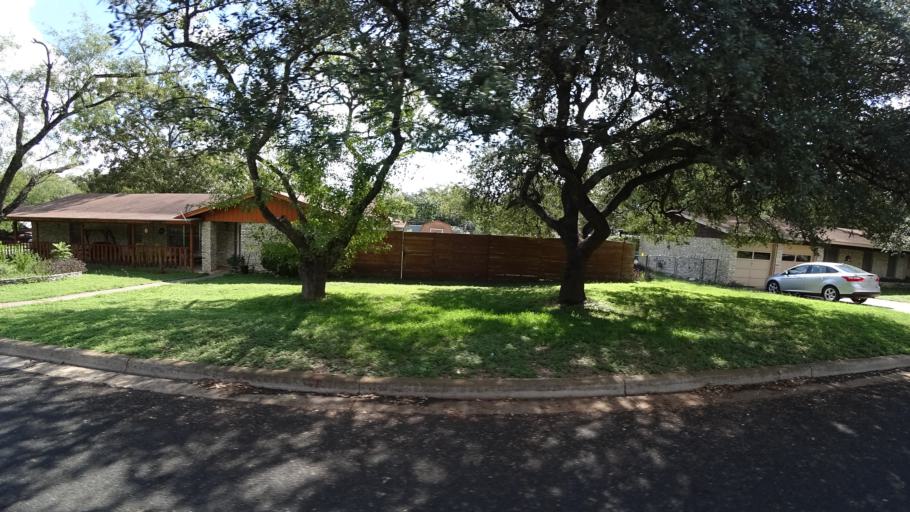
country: US
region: Texas
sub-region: Travis County
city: Shady Hollow
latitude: 30.2018
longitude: -97.8100
